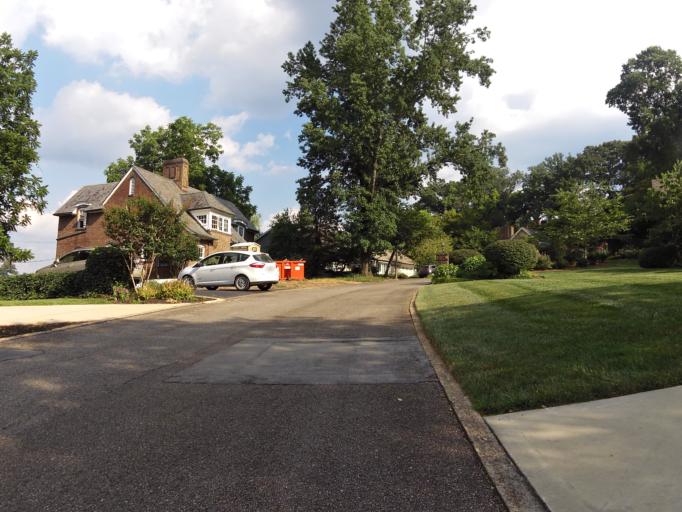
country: US
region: Tennessee
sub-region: Knox County
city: Knoxville
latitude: 35.9432
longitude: -83.9585
